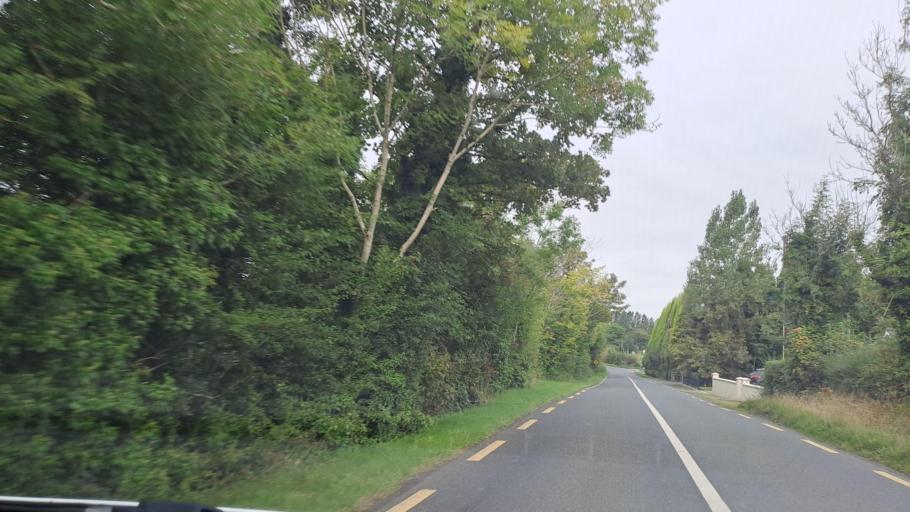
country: IE
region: Ulster
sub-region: An Cabhan
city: Kingscourt
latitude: 53.8970
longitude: -6.7670
